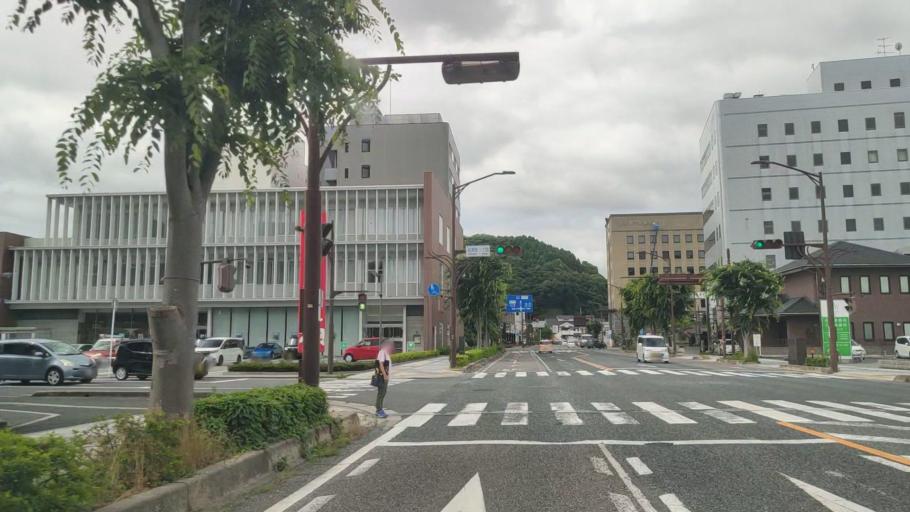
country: JP
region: Tottori
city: Yonago
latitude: 35.4282
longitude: 133.3300
